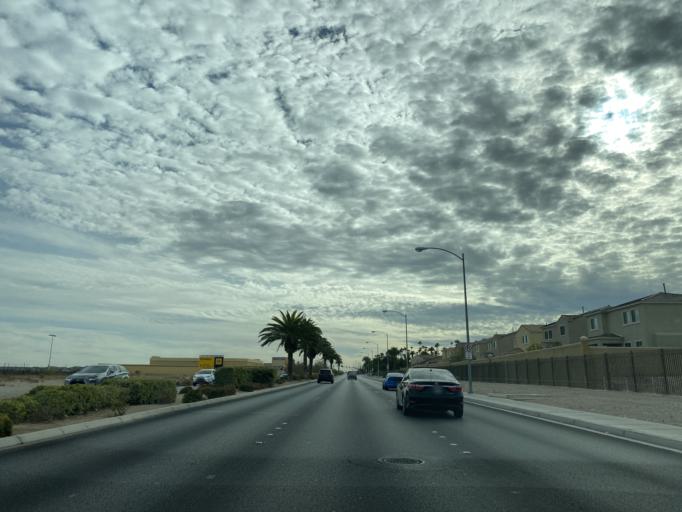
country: US
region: Nevada
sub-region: Clark County
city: Enterprise
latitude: 36.0522
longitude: -115.2792
